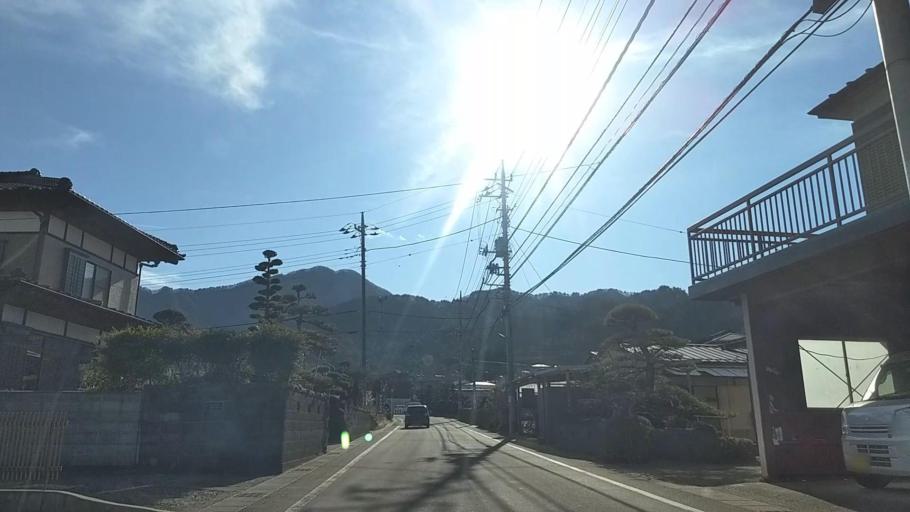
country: JP
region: Yamanashi
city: Otsuki
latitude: 35.5402
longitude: 138.9079
